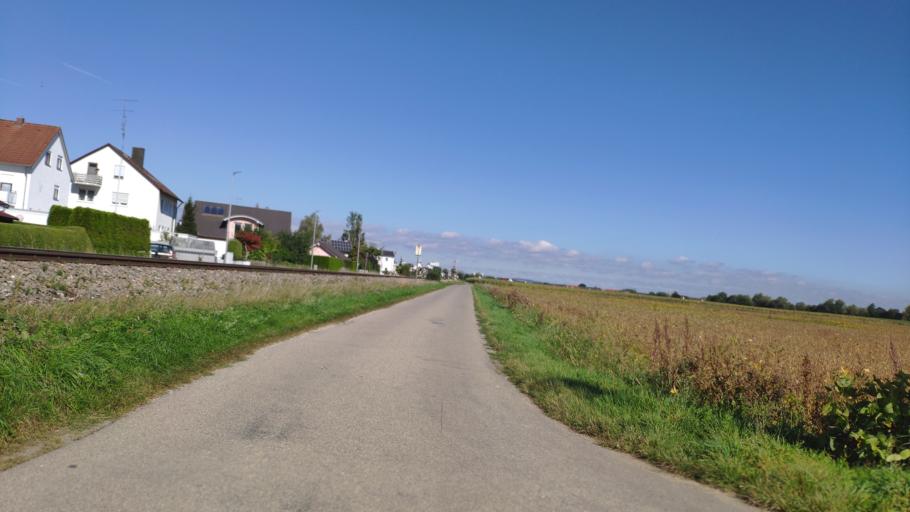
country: DE
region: Bavaria
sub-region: Swabia
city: Senden
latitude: 48.3416
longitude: 10.0401
